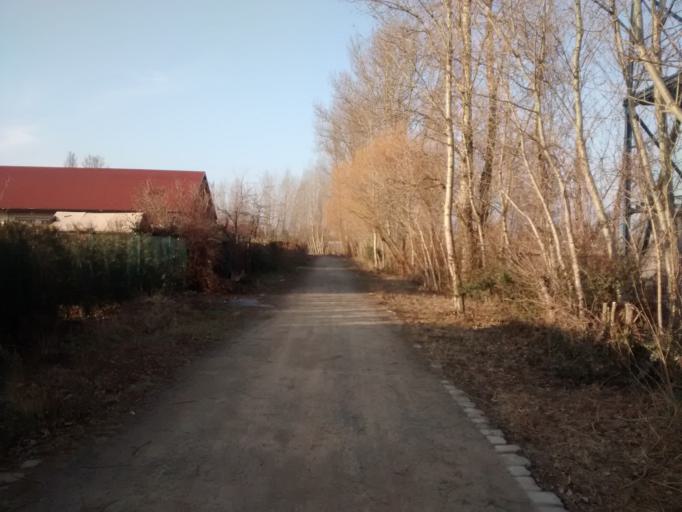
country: DE
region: Berlin
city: Charlottenburg-Nord
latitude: 52.5336
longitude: 13.3121
